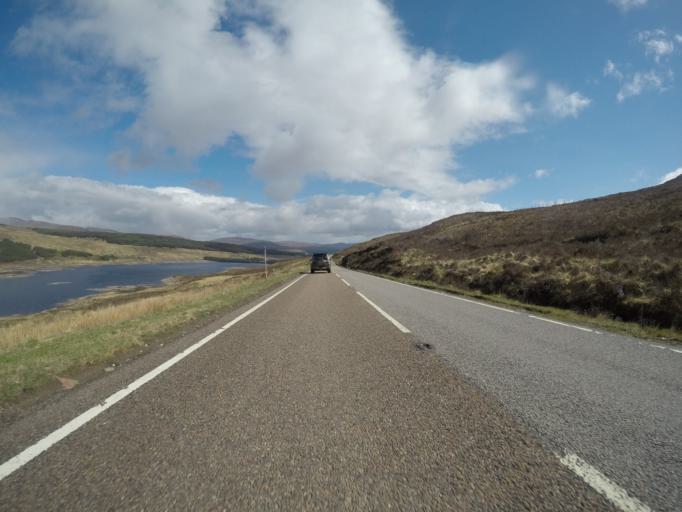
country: GB
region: Scotland
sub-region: Highland
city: Spean Bridge
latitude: 57.1170
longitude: -4.9810
